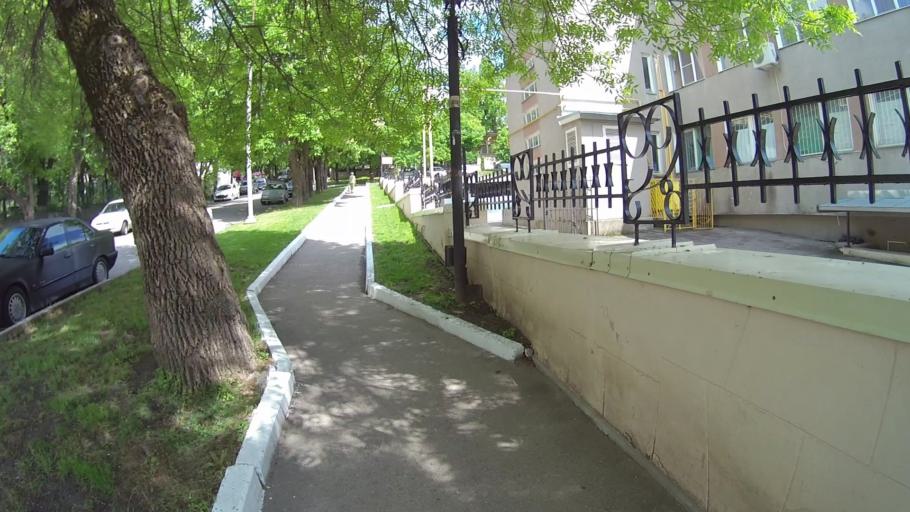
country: RU
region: Stavropol'skiy
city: Pyatigorsk
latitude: 44.0422
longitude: 43.0801
